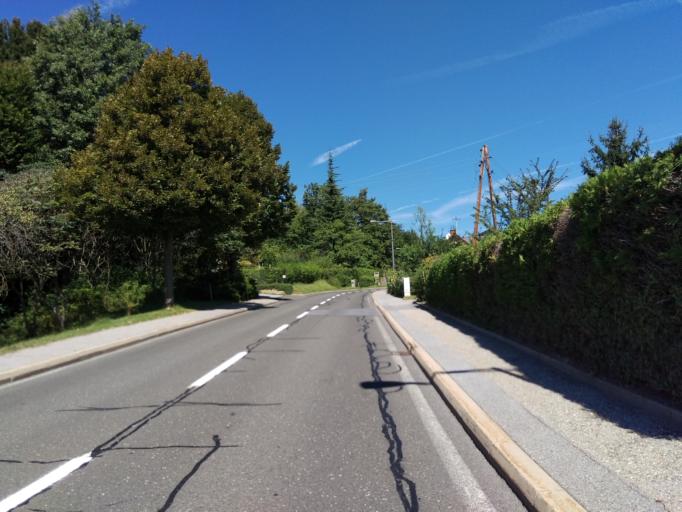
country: AT
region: Styria
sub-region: Politischer Bezirk Graz-Umgebung
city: Nestelbach bei Graz
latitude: 47.0665
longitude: 15.5885
